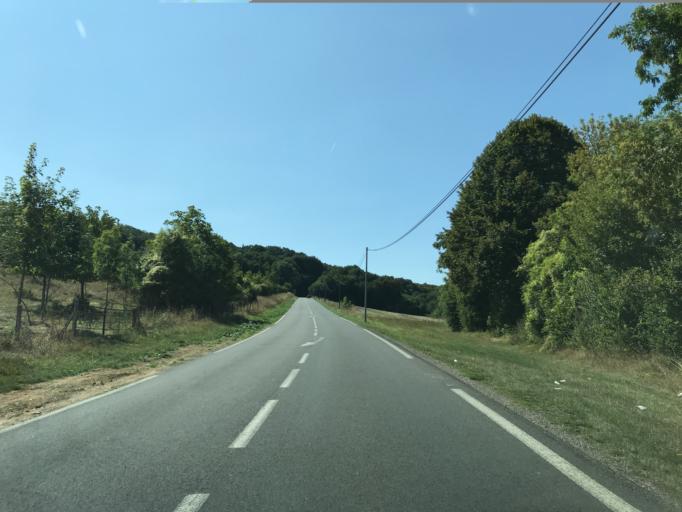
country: FR
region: Haute-Normandie
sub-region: Departement de l'Eure
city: Houlbec-Cocherel
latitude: 49.0643
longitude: 1.2839
